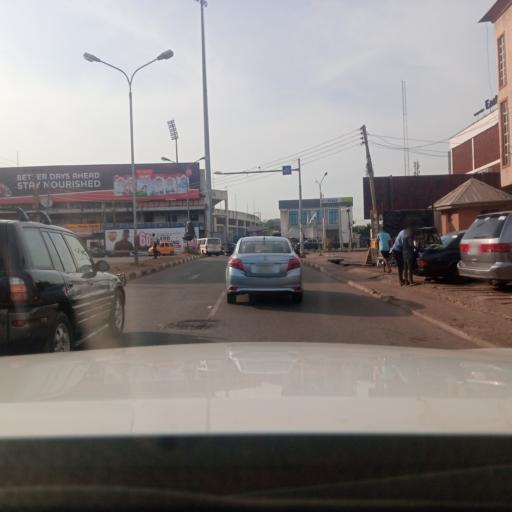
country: NG
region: Enugu
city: Enugu
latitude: 6.4442
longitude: 7.4982
